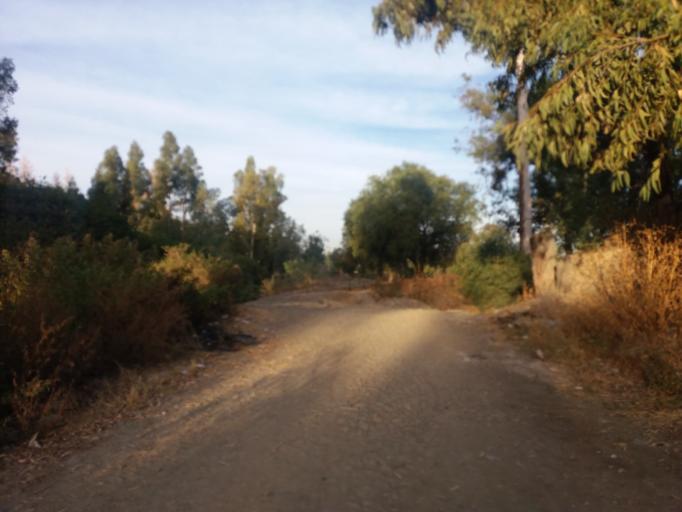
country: BO
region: Cochabamba
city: Cochabamba
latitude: -17.3568
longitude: -66.2030
